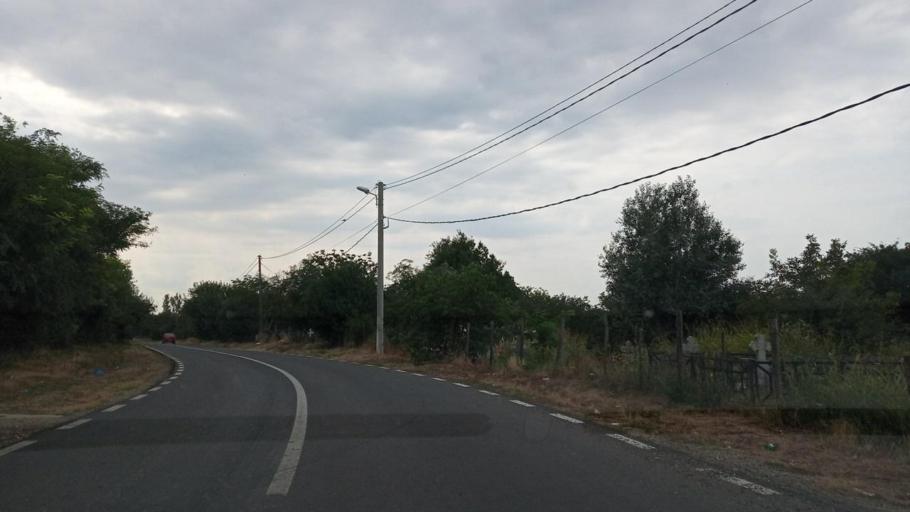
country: RO
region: Giurgiu
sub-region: Comuna Gostinari
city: Gostinari
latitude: 44.1739
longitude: 26.2447
